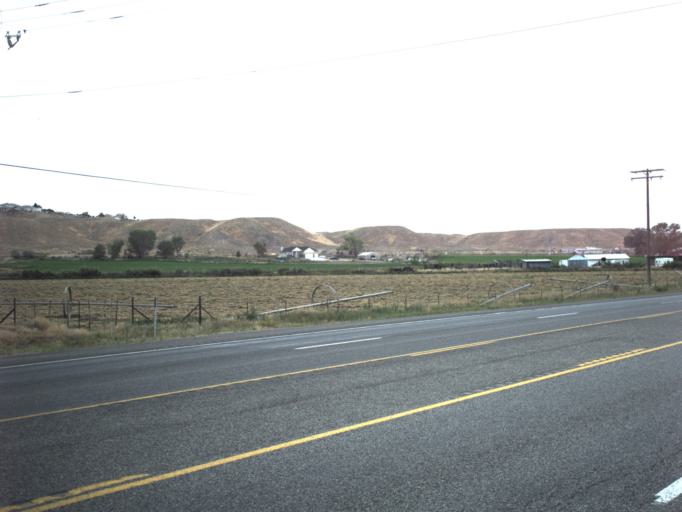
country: US
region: Utah
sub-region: Carbon County
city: Wellington
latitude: 39.5601
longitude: -110.7664
